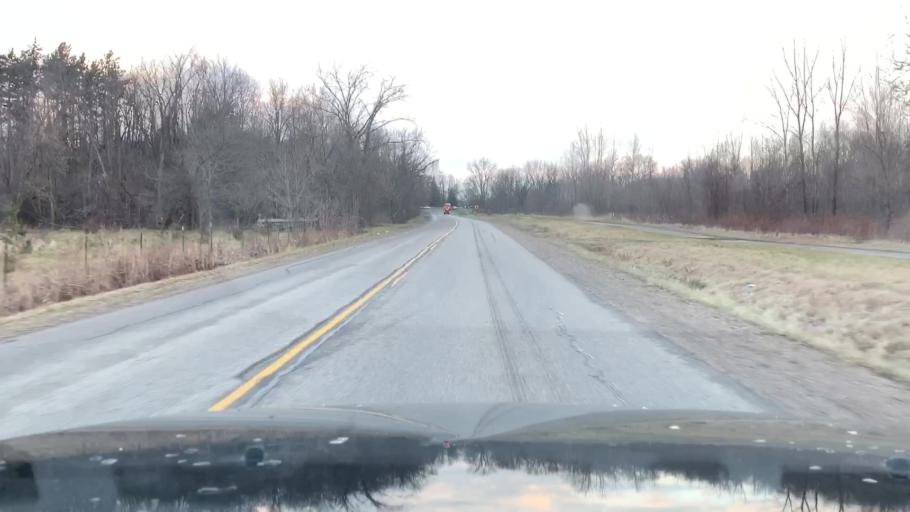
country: US
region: Michigan
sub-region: Ottawa County
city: Zeeland
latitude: 42.7801
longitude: -86.0379
